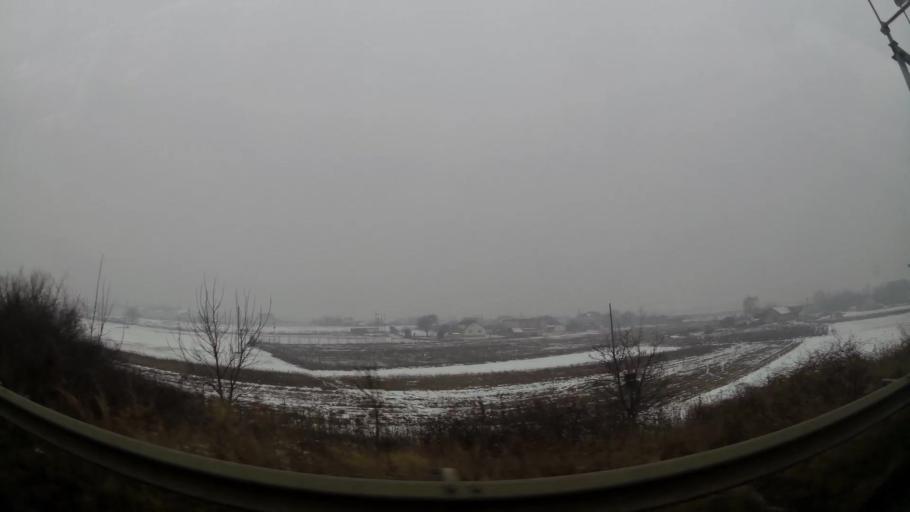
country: MK
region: Petrovec
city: Petrovec
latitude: 41.9428
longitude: 21.6291
